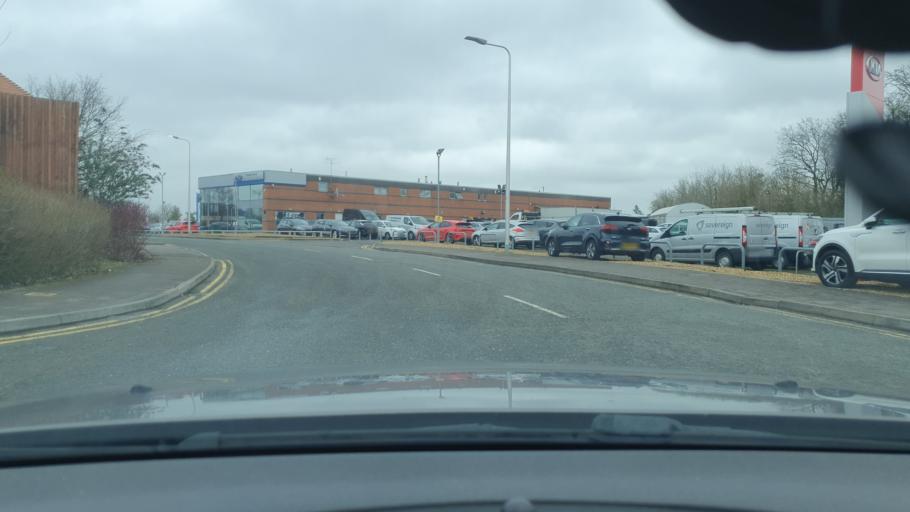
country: GB
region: England
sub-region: West Berkshire
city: Greenham
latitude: 51.3821
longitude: -1.3171
